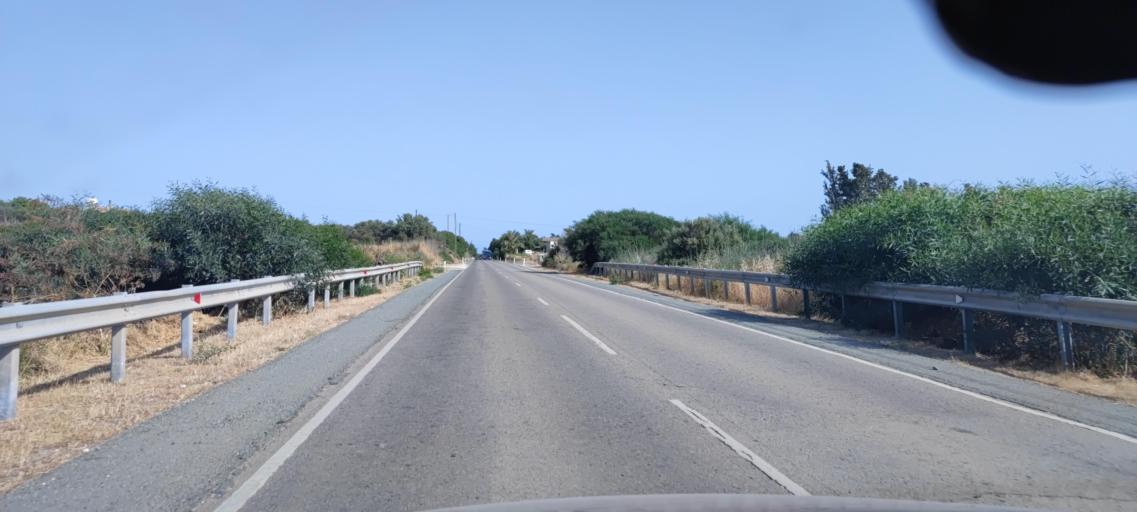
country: CY
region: Limassol
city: Pissouri
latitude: 34.6994
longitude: 32.5746
